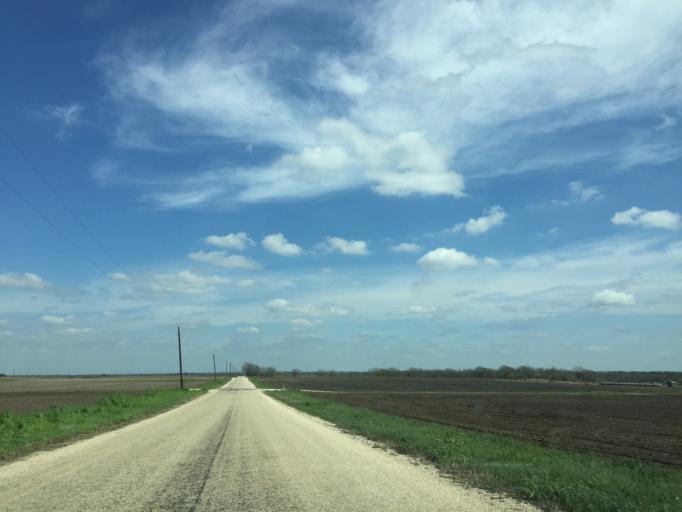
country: US
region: Texas
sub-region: Milam County
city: Thorndale
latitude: 30.5554
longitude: -97.2517
